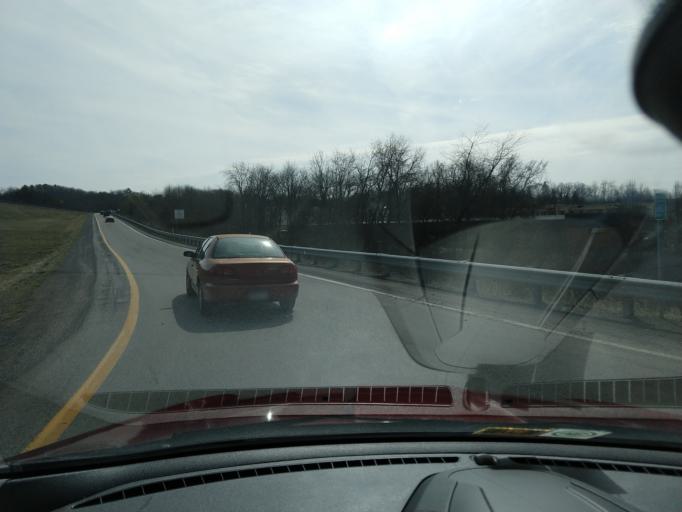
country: US
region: West Virginia
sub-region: Greenbrier County
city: Lewisburg
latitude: 37.8149
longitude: -80.4260
